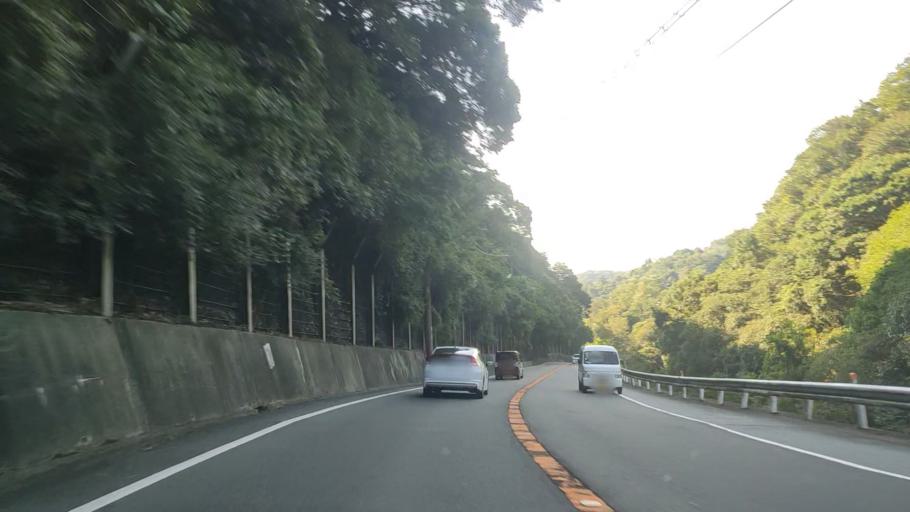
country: JP
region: Hyogo
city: Kobe
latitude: 34.7149
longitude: 135.1595
